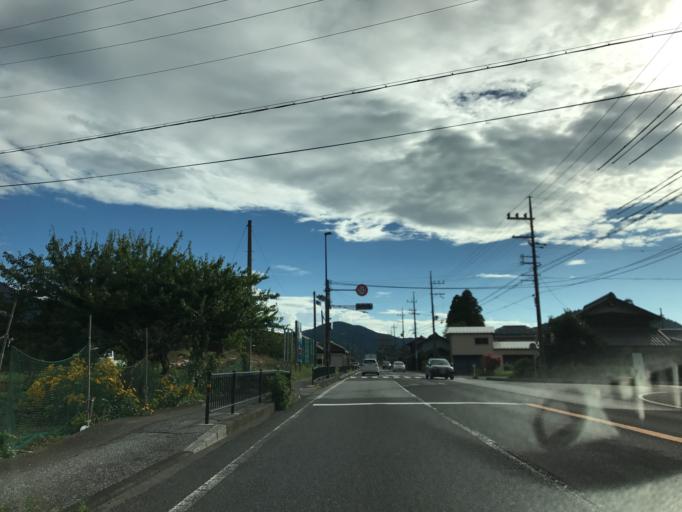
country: JP
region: Gifu
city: Tarui
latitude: 35.3431
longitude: 136.4060
